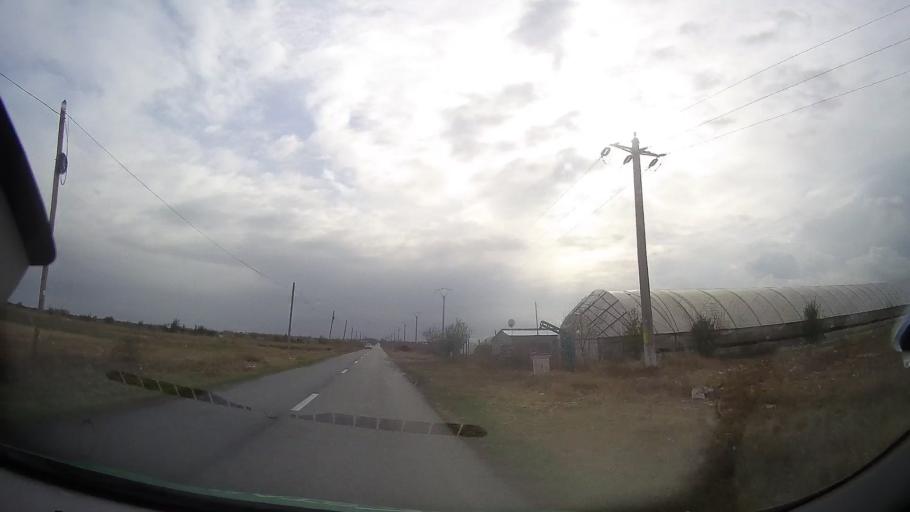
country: RO
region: Ialomita
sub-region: Comuna Fierbinti-Targ
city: Fierbintii de Jos
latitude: 44.7112
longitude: 26.3912
